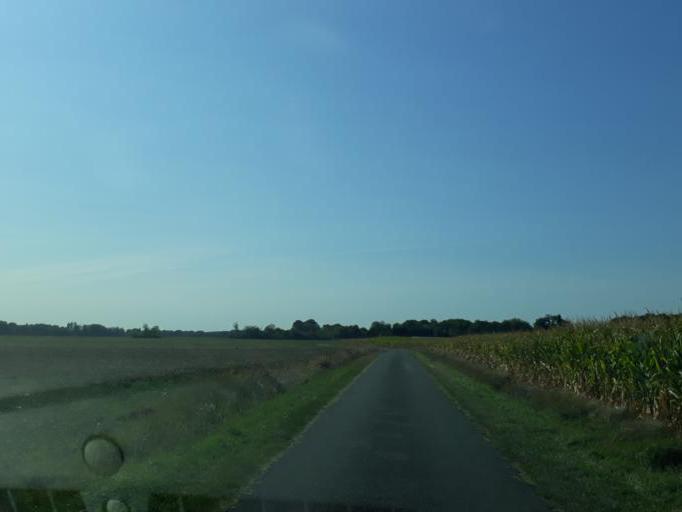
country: FR
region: Centre
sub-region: Departement du Loir-et-Cher
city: Selles-sur-Cher
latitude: 47.2693
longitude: 1.5787
